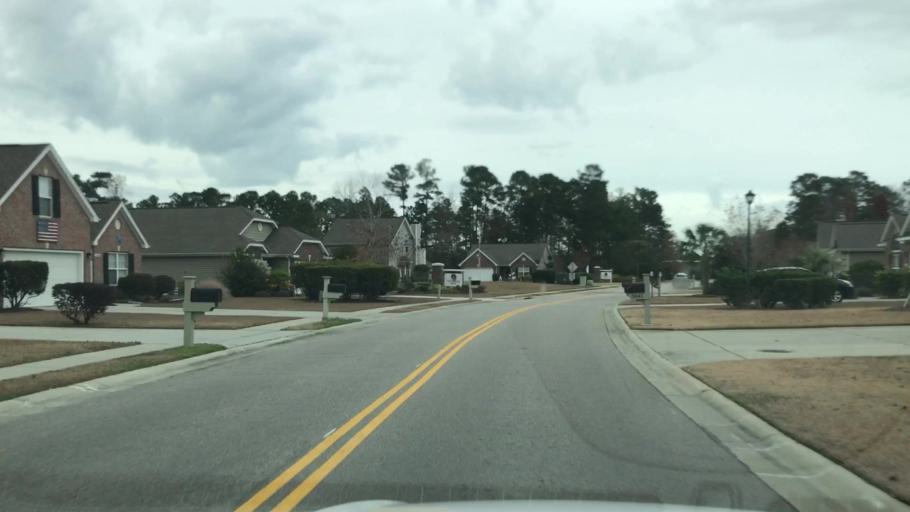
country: US
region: South Carolina
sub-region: Horry County
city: Forestbrook
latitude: 33.7144
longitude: -78.9418
